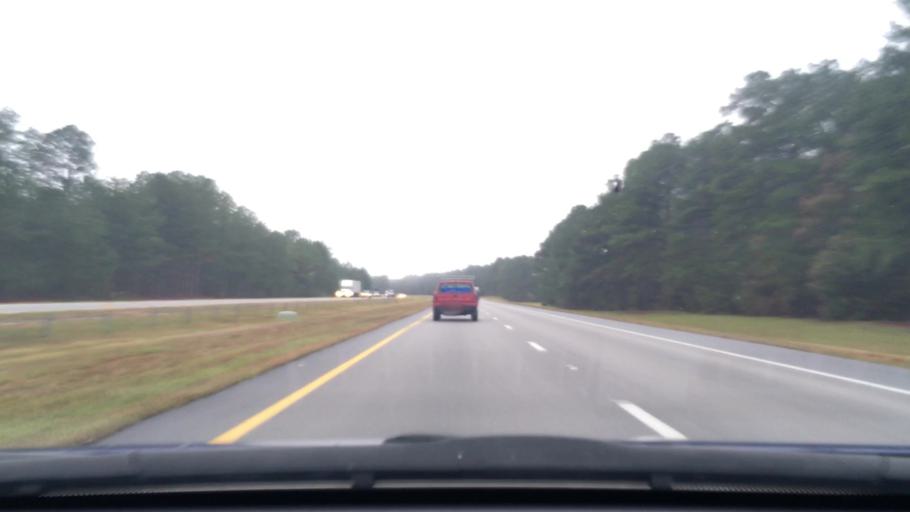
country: US
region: South Carolina
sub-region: Lee County
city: Bishopville
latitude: 34.1985
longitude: -80.3417
